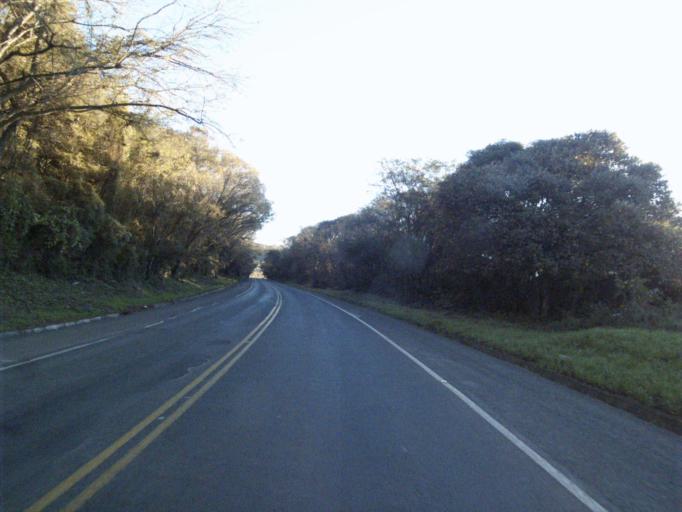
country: BR
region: Santa Catarina
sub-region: Chapeco
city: Chapeco
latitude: -26.8307
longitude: -53.0265
